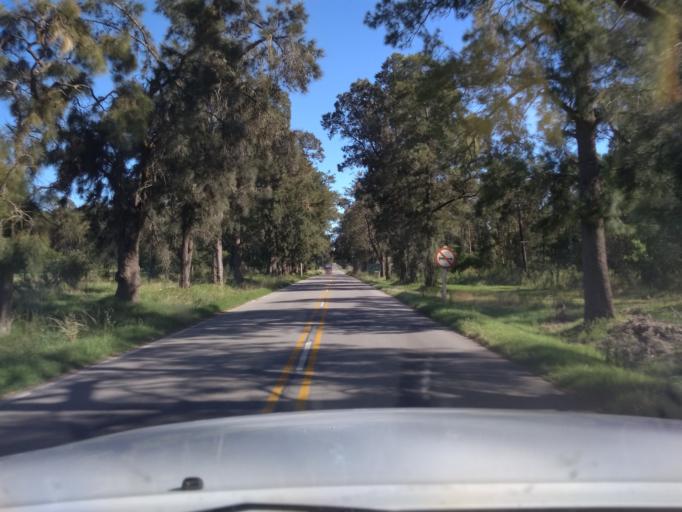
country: UY
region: Canelones
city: San Bautista
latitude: -34.3818
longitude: -55.9595
